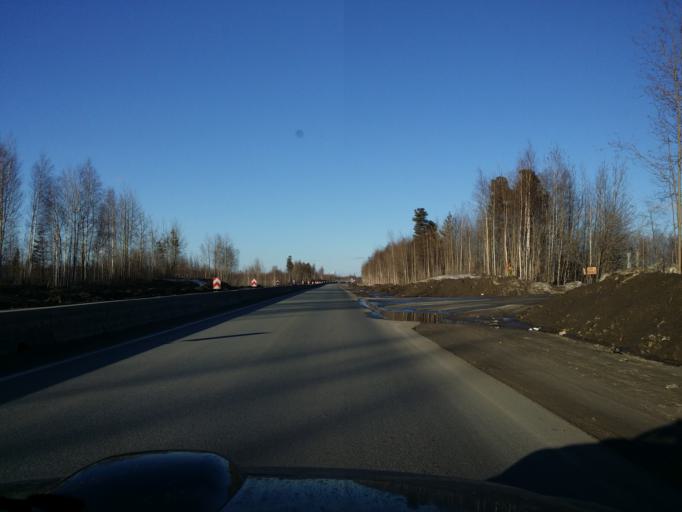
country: RU
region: Khanty-Mansiyskiy Avtonomnyy Okrug
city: Megion
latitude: 61.0559
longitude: 76.1532
